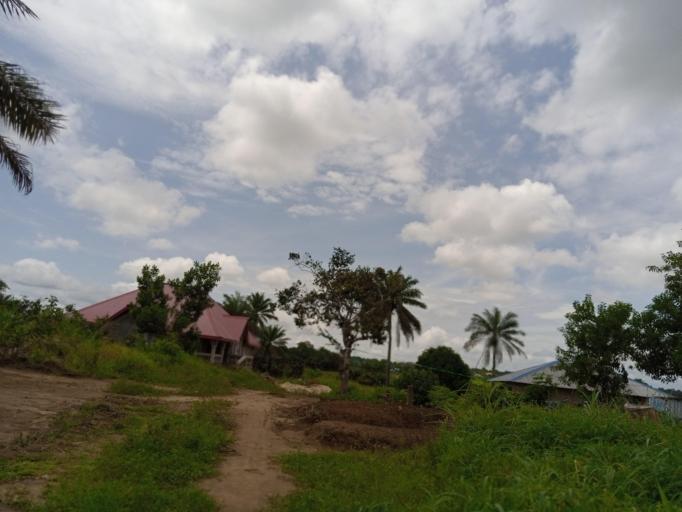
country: SL
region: Northern Province
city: Masoyila
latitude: 8.5921
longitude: -13.1804
